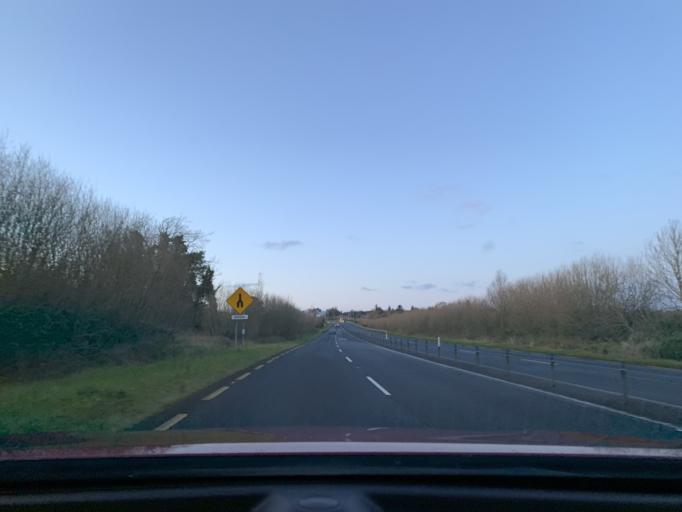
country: IE
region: Connaught
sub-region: County Leitrim
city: Carrick-on-Shannon
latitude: 53.8766
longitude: -7.9312
